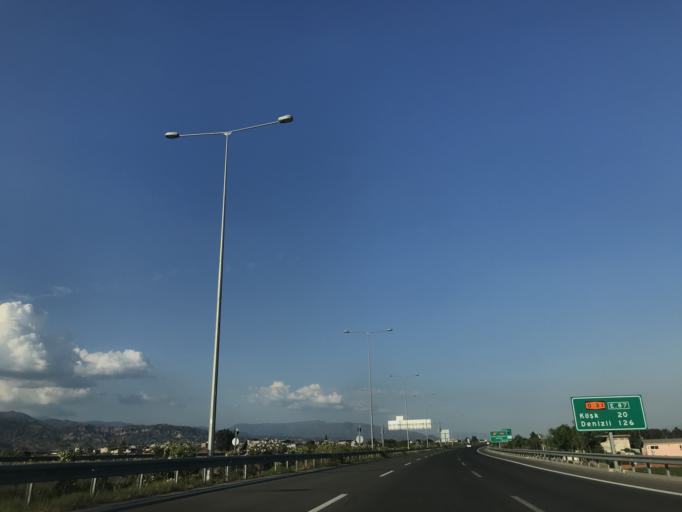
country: TR
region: Aydin
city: Tepecik
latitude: 37.8189
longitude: 27.8683
